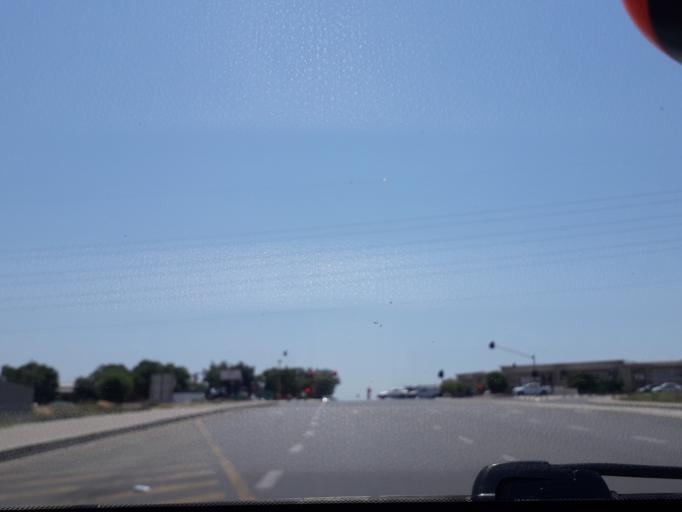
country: ZA
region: Gauteng
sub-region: City of Johannesburg Metropolitan Municipality
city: Midrand
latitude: -26.0155
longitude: 28.1284
